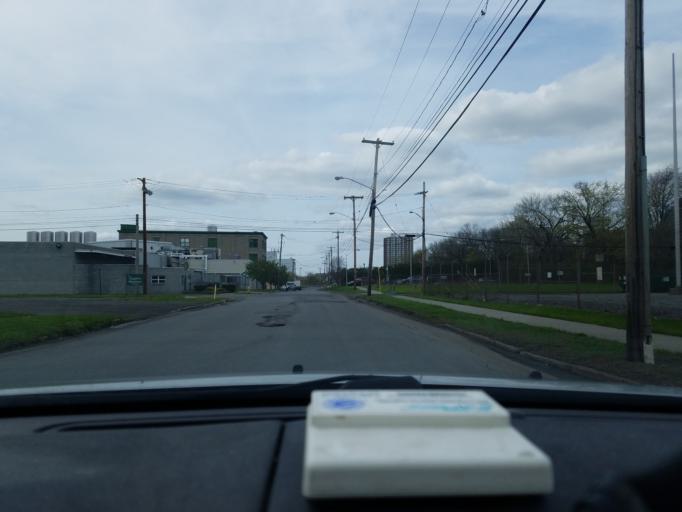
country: US
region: New York
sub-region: Onondaga County
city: Syracuse
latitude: 43.0399
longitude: -76.1528
